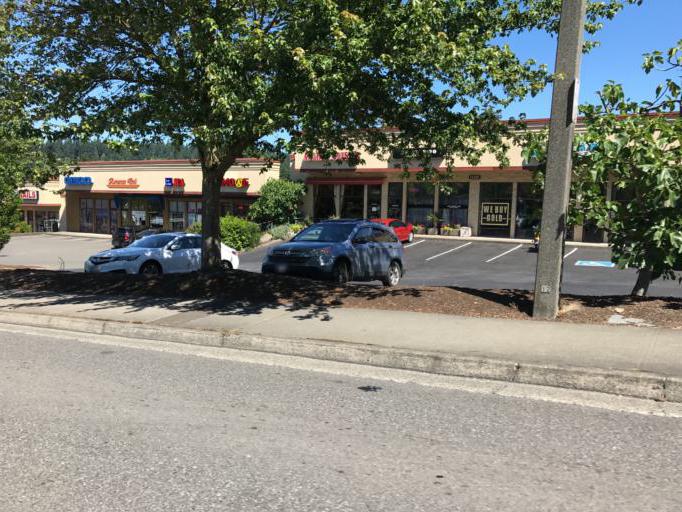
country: US
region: Washington
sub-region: King County
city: Redmond
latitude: 47.6280
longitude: -122.1491
